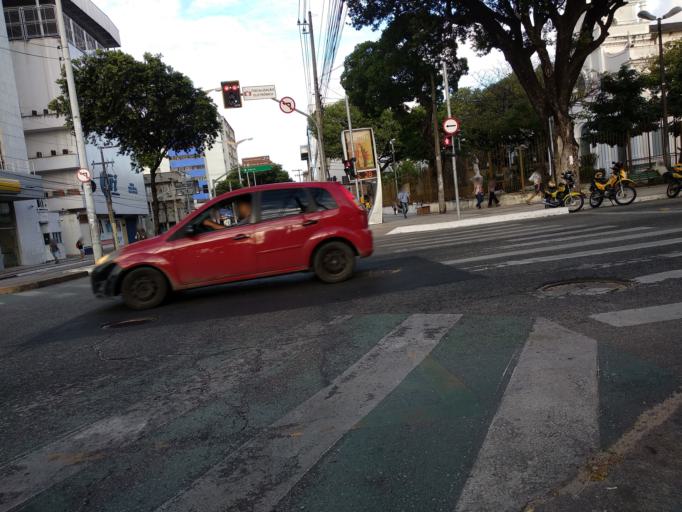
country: BR
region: Ceara
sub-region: Fortaleza
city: Fortaleza
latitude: -3.7316
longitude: -38.5305
